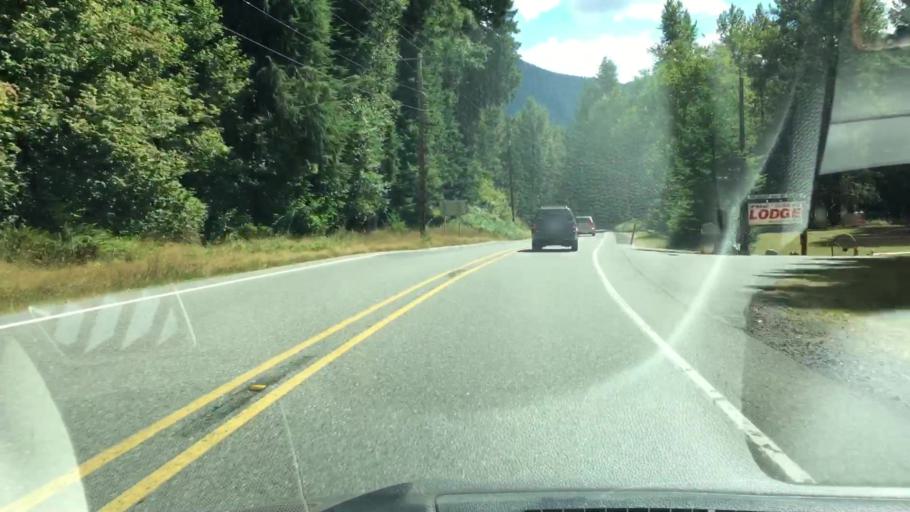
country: US
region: Washington
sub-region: Pierce County
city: Eatonville
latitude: 46.7453
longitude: -121.9237
